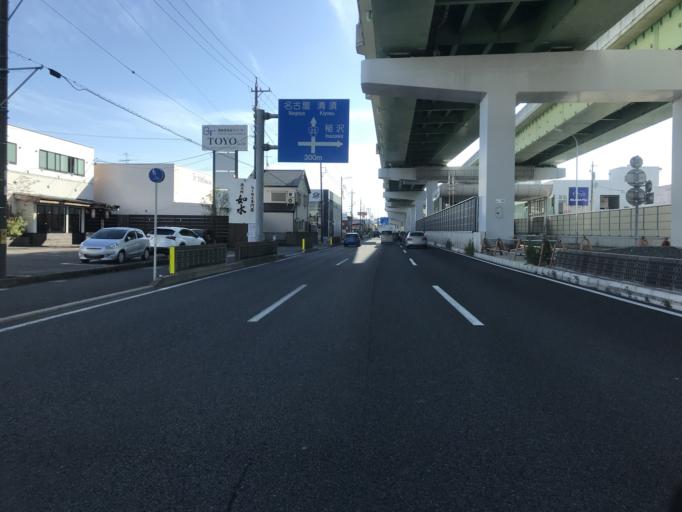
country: JP
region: Aichi
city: Iwakura
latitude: 35.2499
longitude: 136.8444
